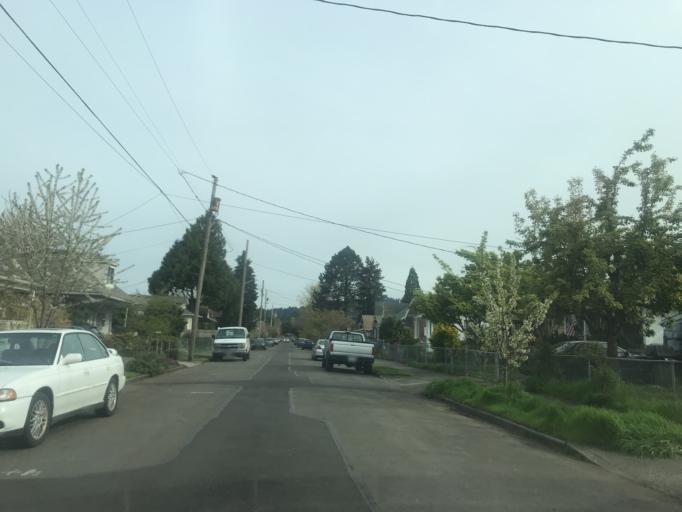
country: US
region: Oregon
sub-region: Multnomah County
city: Lents
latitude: 45.4926
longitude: -122.5974
